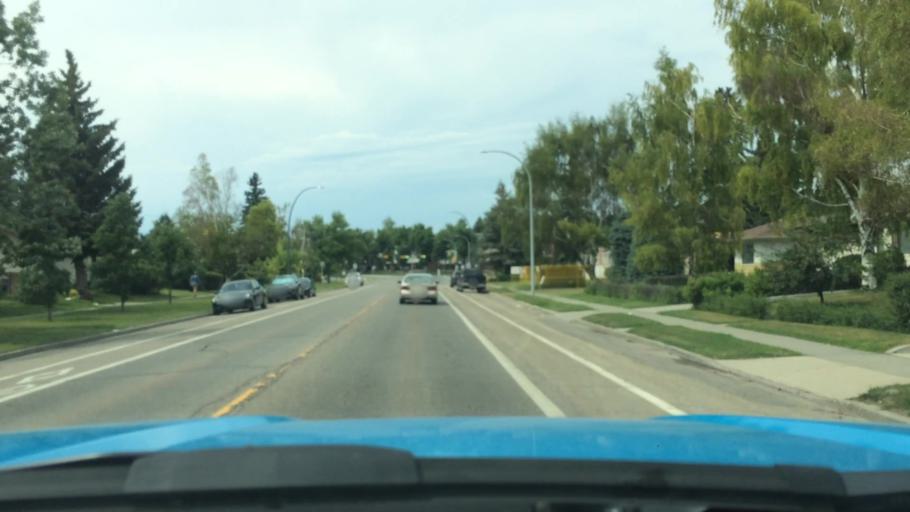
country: CA
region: Alberta
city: Calgary
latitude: 51.0816
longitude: -114.0902
